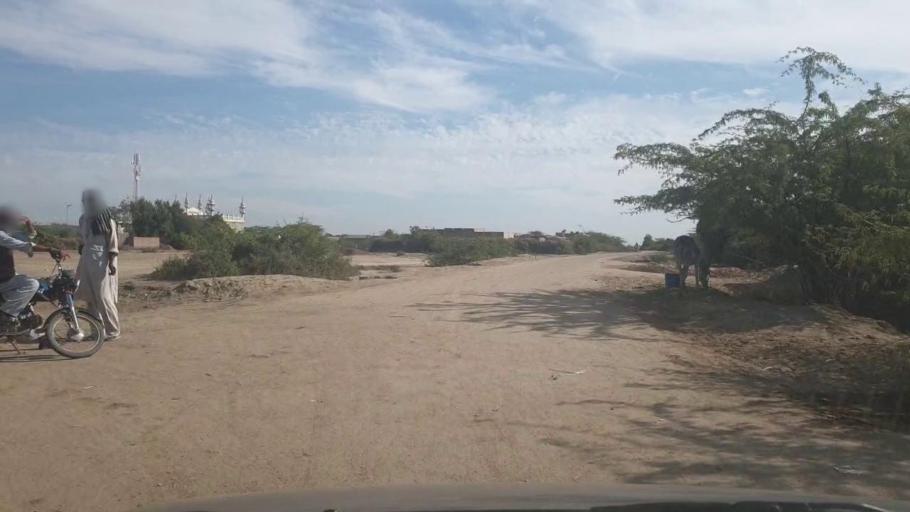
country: PK
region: Sindh
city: Pithoro
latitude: 25.3982
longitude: 69.2512
